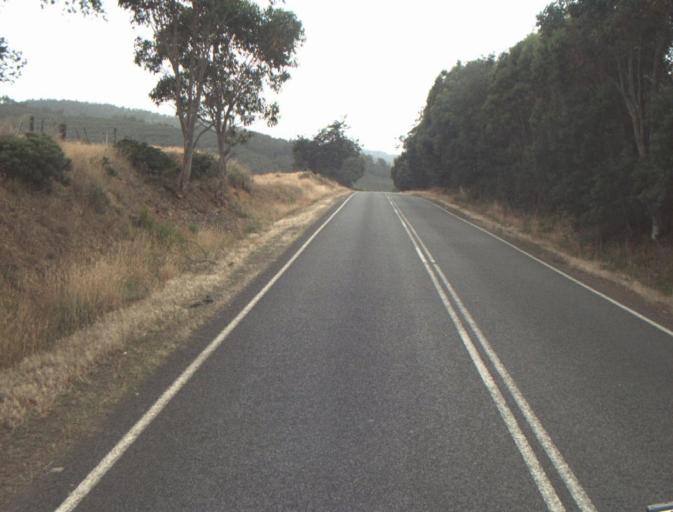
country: AU
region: Tasmania
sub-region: Northern Midlands
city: Evandale
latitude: -41.4740
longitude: 147.5426
